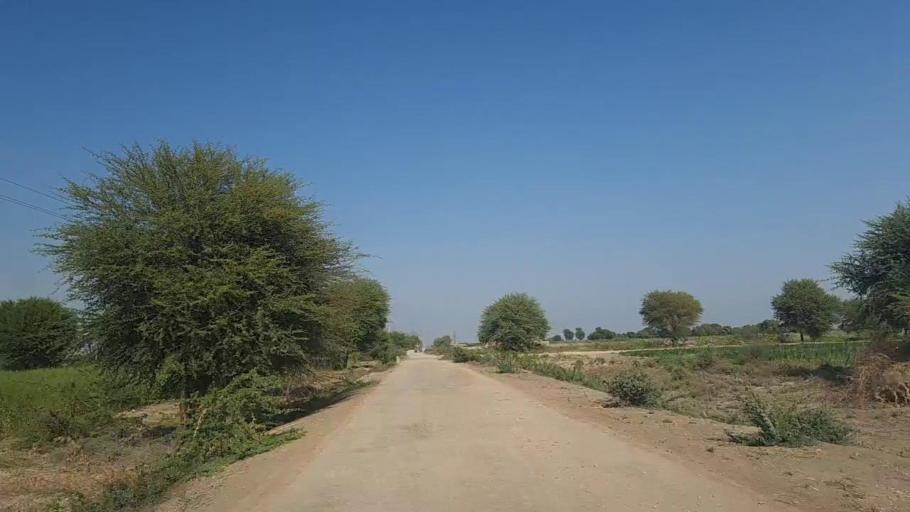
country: PK
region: Sindh
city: Digri
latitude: 25.0914
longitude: 69.2028
